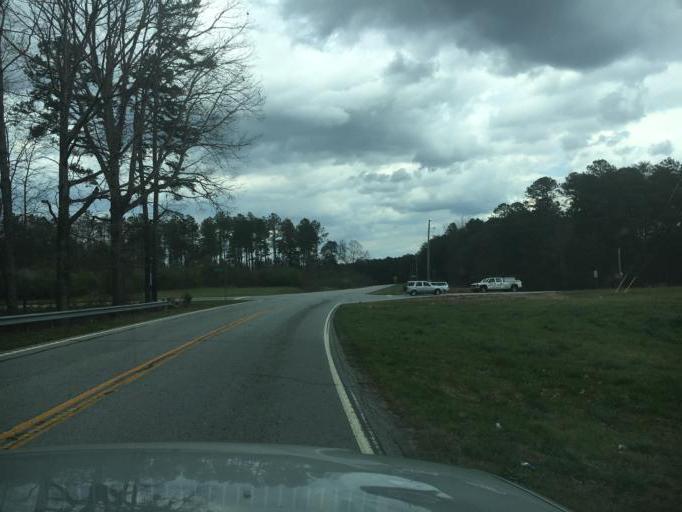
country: US
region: South Carolina
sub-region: Oconee County
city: Westminster
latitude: 34.6973
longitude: -83.0792
